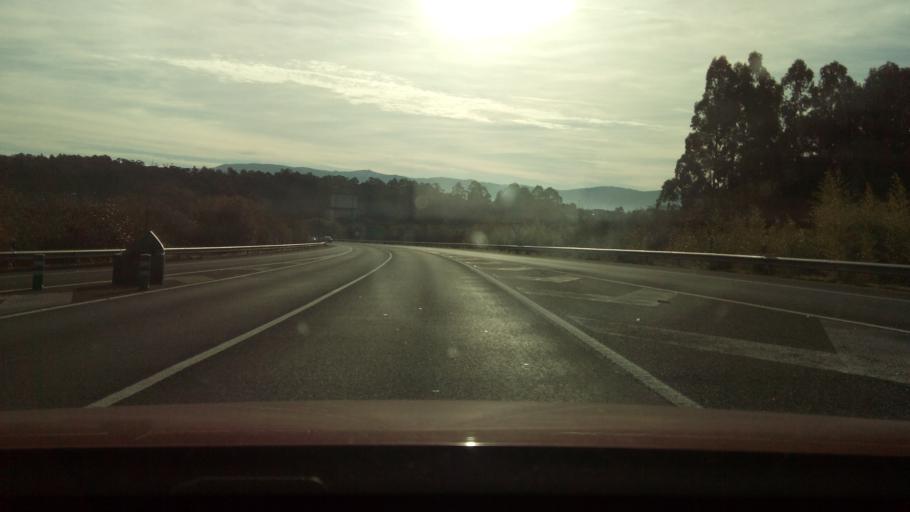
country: ES
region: Galicia
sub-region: Provincia de Pontevedra
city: Sanxenxo
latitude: 42.4156
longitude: -8.8274
